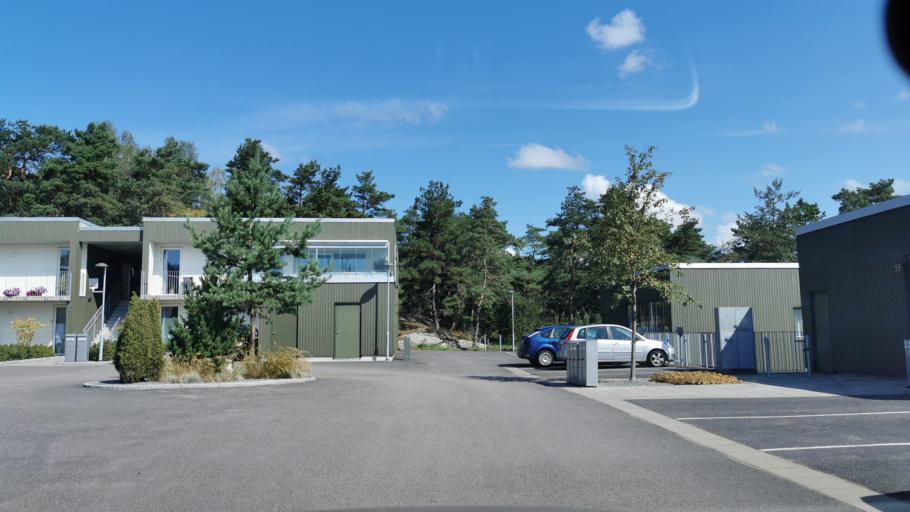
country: SE
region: Vaestra Goetaland
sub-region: Goteborg
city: Majorna
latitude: 57.6569
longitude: 11.9107
